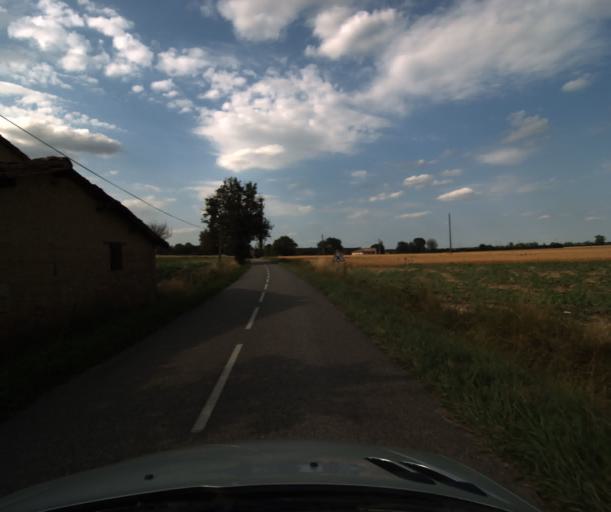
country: FR
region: Midi-Pyrenees
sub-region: Departement de la Haute-Garonne
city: Fonsorbes
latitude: 43.5250
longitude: 1.2322
